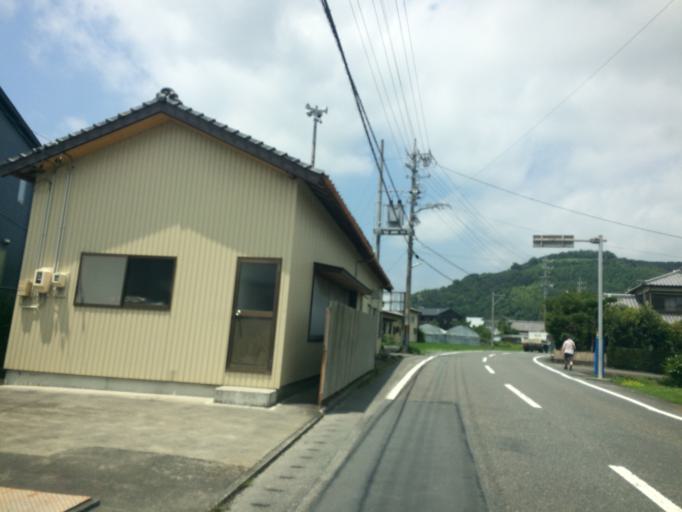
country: JP
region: Shizuoka
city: Shimada
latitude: 34.8337
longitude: 138.2021
